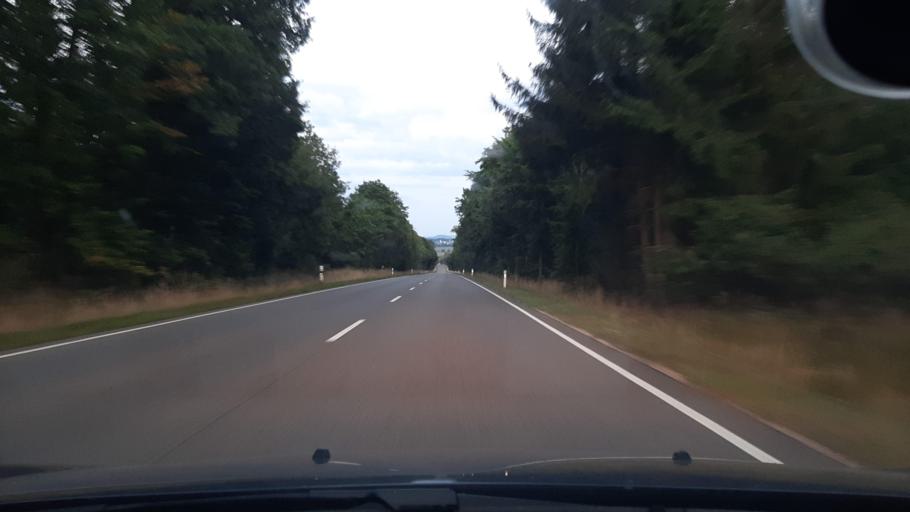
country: DE
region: North Rhine-Westphalia
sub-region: Regierungsbezirk Koln
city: Nettersheim
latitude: 50.4487
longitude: 6.5753
